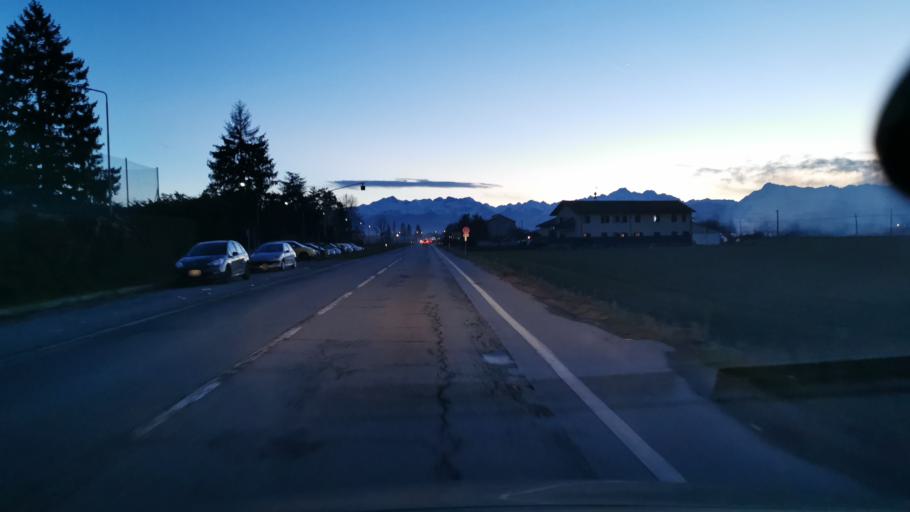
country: IT
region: Piedmont
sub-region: Provincia di Cuneo
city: Roata Rossi
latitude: 44.4389
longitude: 7.5633
